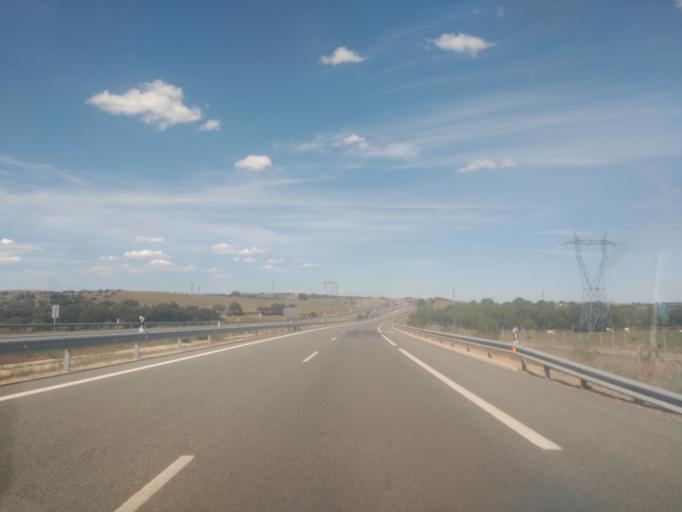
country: ES
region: Castille and Leon
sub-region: Provincia de Salamanca
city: Guijuelo
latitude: 40.5279
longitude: -5.6701
